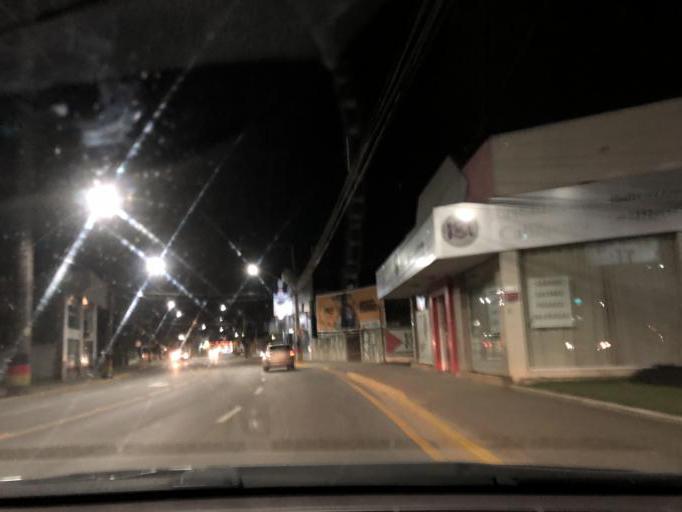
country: BR
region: Santa Catarina
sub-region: Jaragua Do Sul
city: Jaragua do Sul
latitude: -26.5023
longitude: -49.0894
